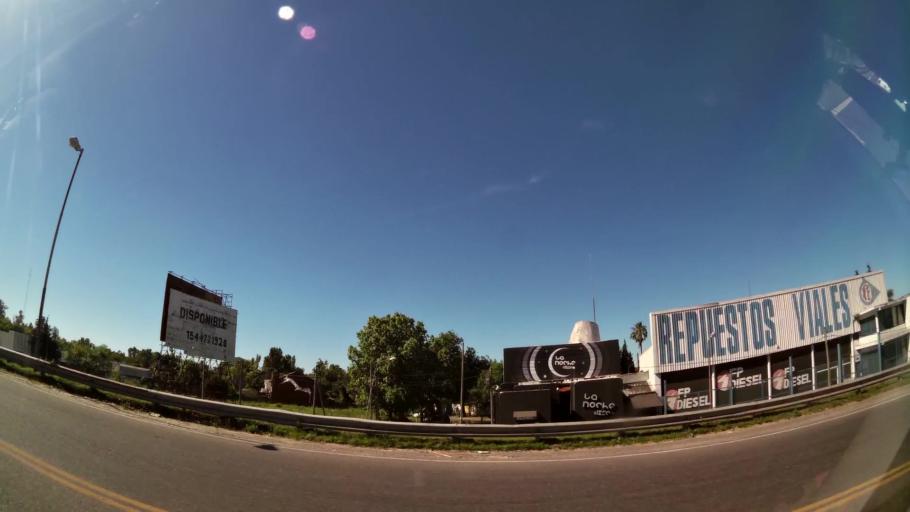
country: AR
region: Buenos Aires
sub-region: Partido de Tigre
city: Tigre
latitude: -34.4826
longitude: -58.6350
